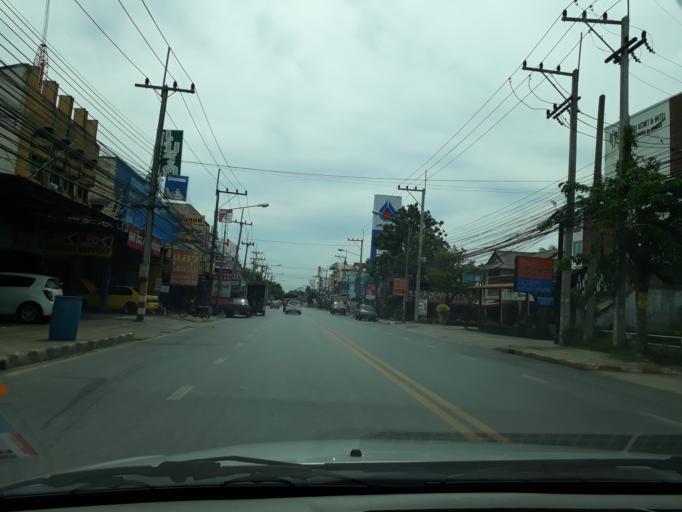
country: TH
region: Khon Kaen
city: Khon Kaen
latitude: 16.4358
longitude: 102.8518
